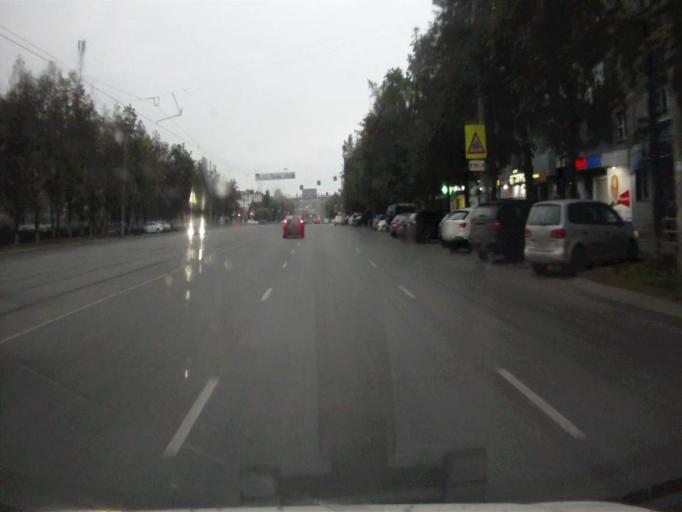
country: RU
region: Chelyabinsk
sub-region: Gorod Chelyabinsk
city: Chelyabinsk
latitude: 55.1774
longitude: 61.3997
